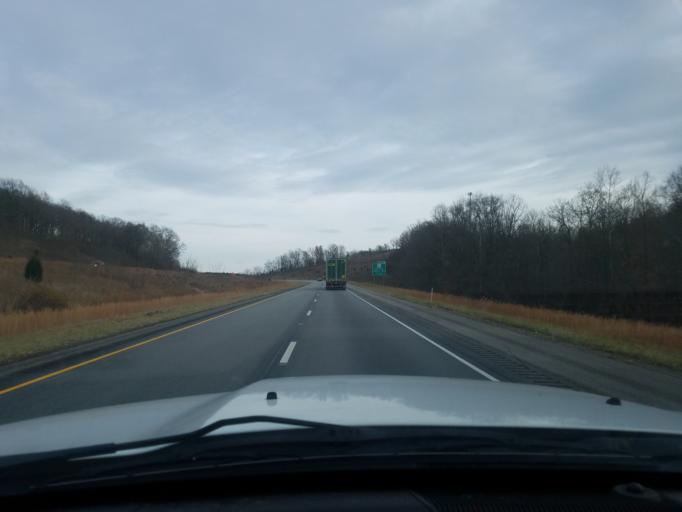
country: US
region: Indiana
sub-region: Crawford County
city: English
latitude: 38.2310
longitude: -86.6186
